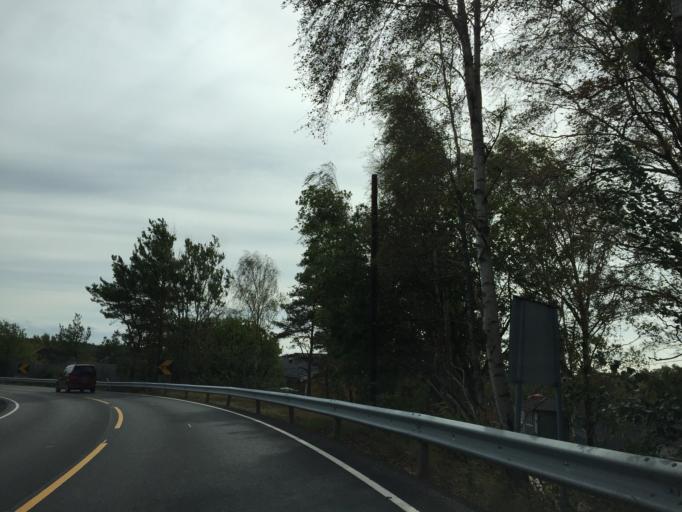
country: NO
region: Ostfold
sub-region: Fredrikstad
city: Fredrikstad
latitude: 59.0984
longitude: 10.9078
